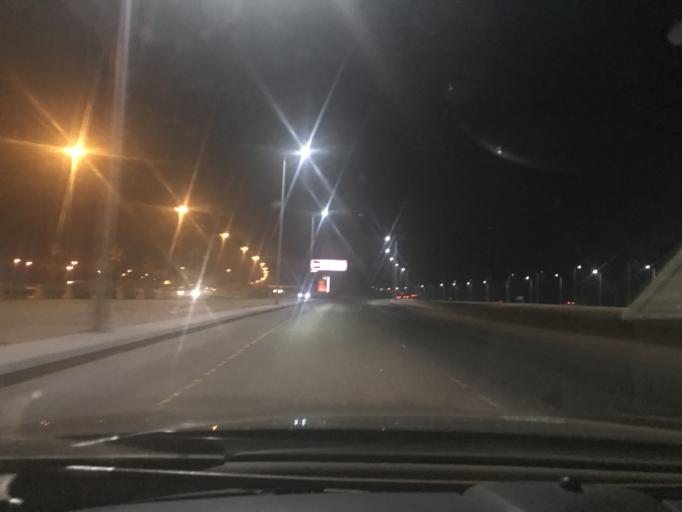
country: SA
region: Ar Riyad
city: Riyadh
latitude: 24.8581
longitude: 46.7333
